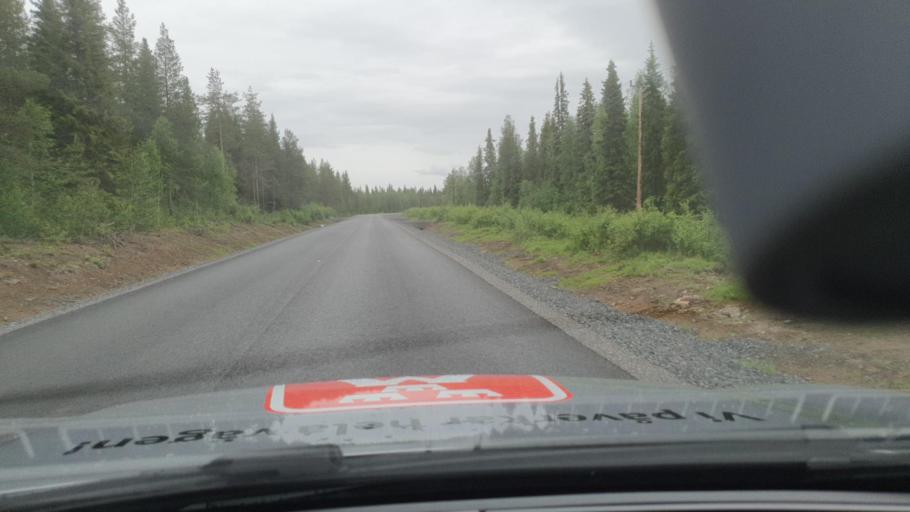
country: SE
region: Norrbotten
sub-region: Overkalix Kommun
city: OEverkalix
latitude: 66.7122
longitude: 23.2010
